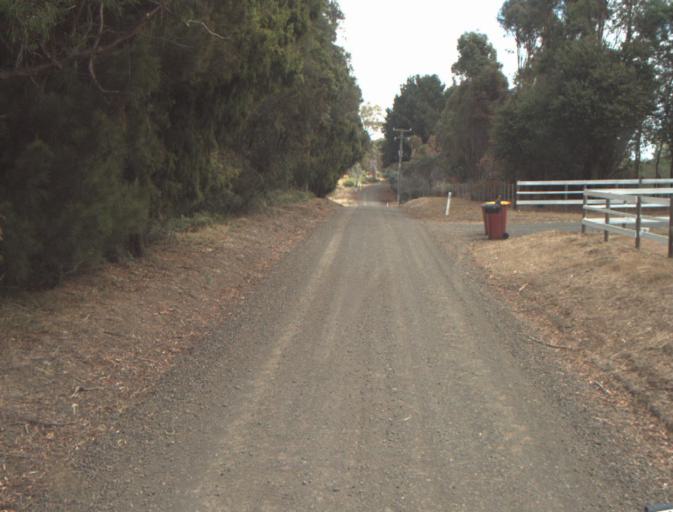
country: AU
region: Tasmania
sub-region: Launceston
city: Mayfield
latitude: -41.2797
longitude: 147.0441
